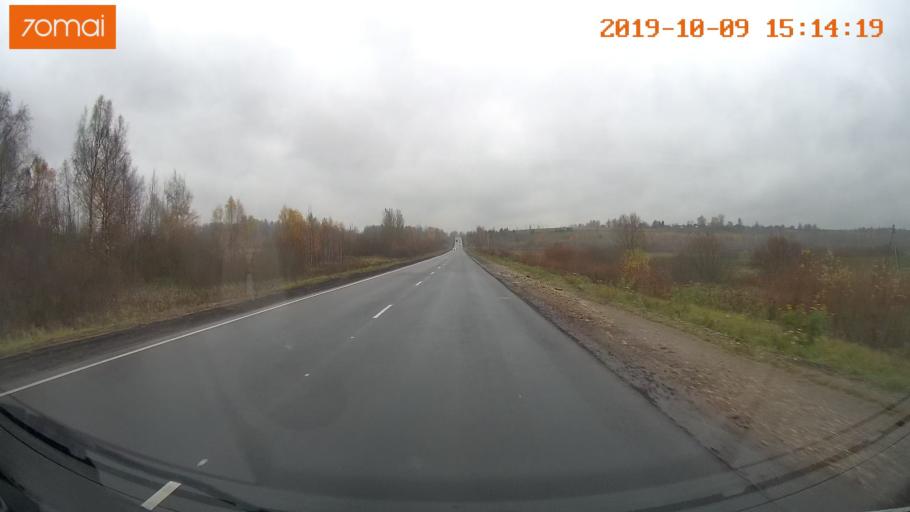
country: RU
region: Kostroma
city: Susanino
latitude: 58.1363
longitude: 41.6046
